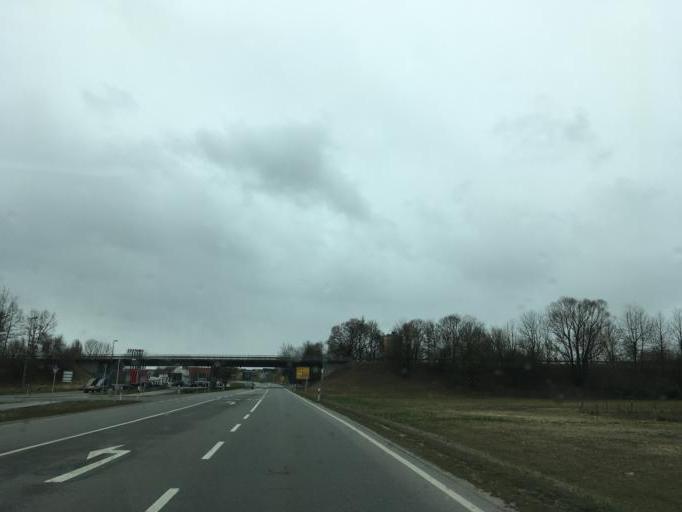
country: DE
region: Bavaria
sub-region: Lower Bavaria
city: Mainburg
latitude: 48.6312
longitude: 11.7777
